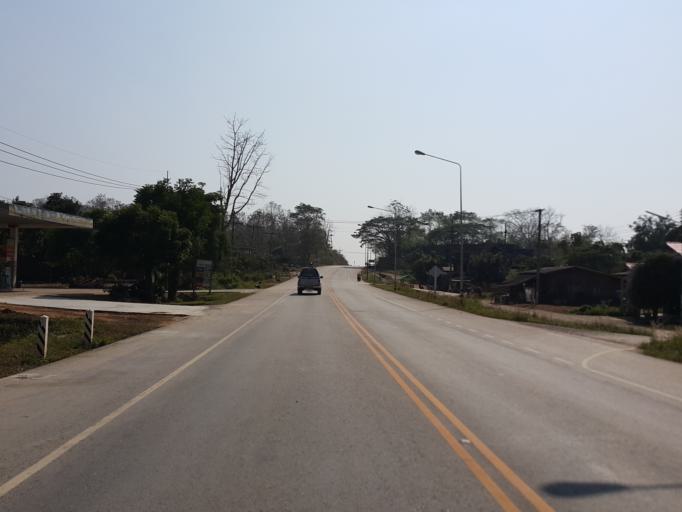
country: TH
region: Lampang
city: Mueang Pan
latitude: 18.9061
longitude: 99.6064
